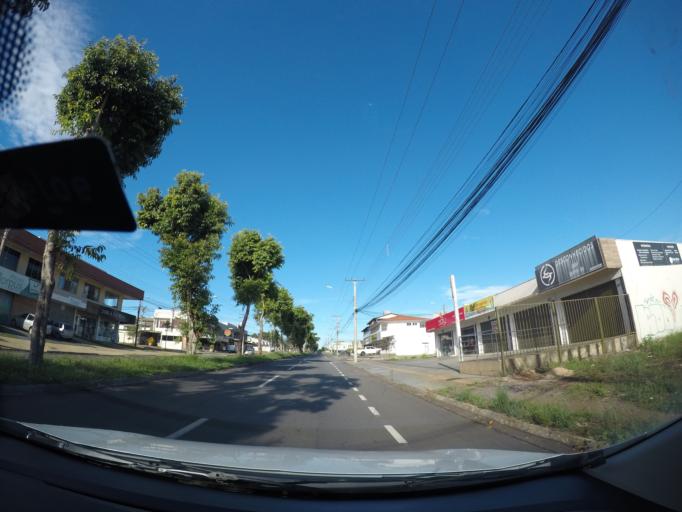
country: BR
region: Goias
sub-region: Goiania
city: Goiania
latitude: -16.7337
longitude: -49.3024
